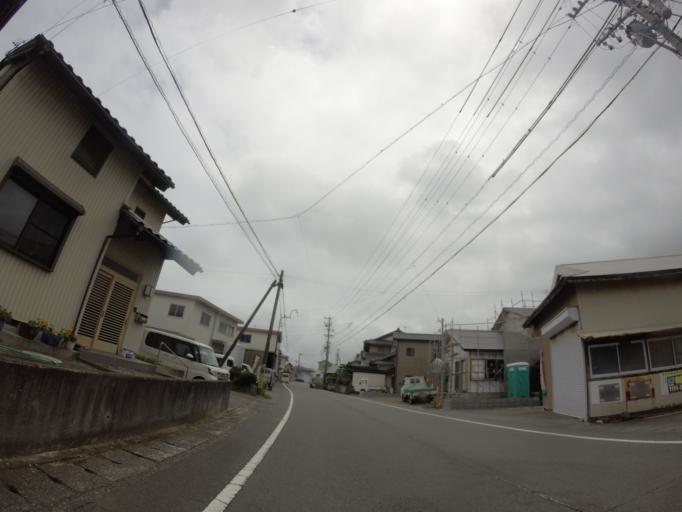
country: JP
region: Shizuoka
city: Sagara
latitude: 34.7263
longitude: 138.2185
